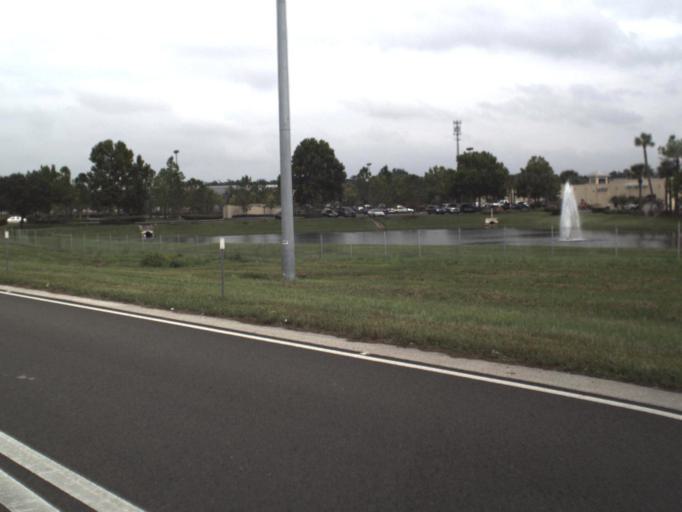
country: US
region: Florida
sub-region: Manatee County
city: Ellenton
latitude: 27.5346
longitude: -82.5098
